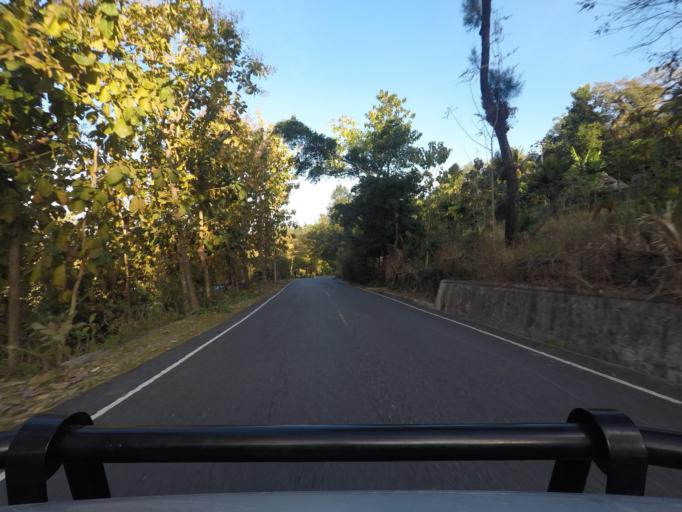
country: TL
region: Bobonaro
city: Maliana
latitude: -8.9556
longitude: 125.0761
